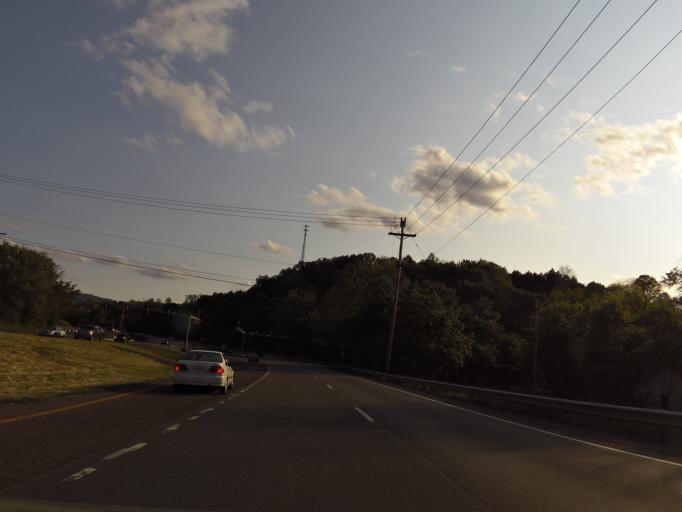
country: US
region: Virginia
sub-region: Tazewell County
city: Claypool Hill
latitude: 37.0388
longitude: -81.7964
